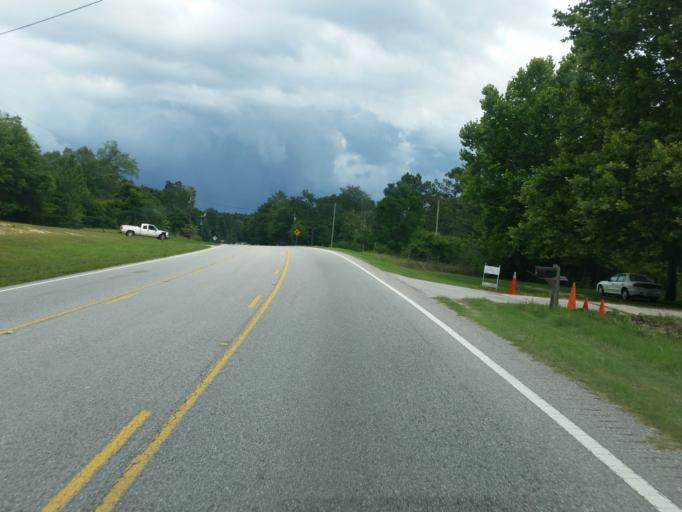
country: US
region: Mississippi
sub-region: George County
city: Lucedale
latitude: 30.8515
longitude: -88.4040
